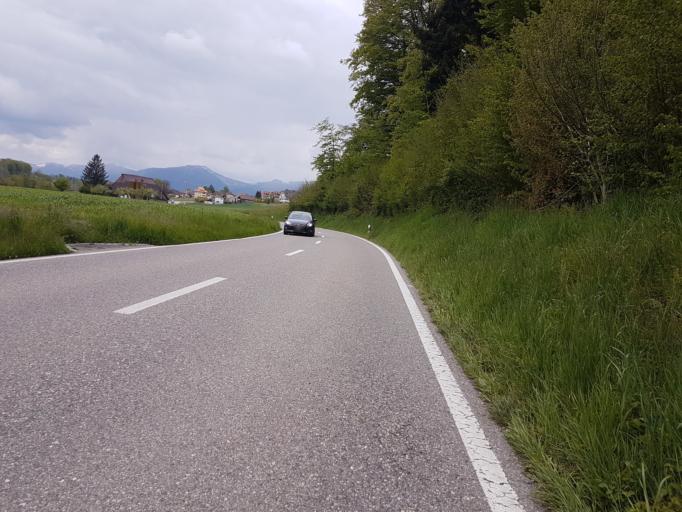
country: CH
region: Bern
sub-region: Oberaargau
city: Niederbipp
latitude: 47.2344
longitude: 7.7009
